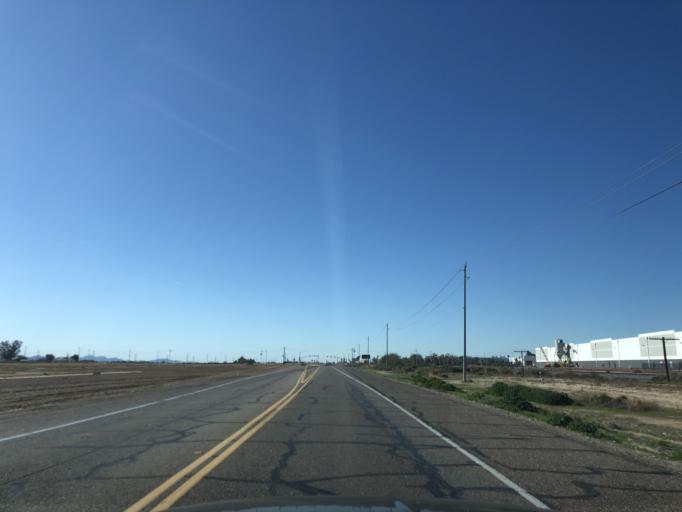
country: US
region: Arizona
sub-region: Maricopa County
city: Goodyear
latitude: 33.4053
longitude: -112.4210
